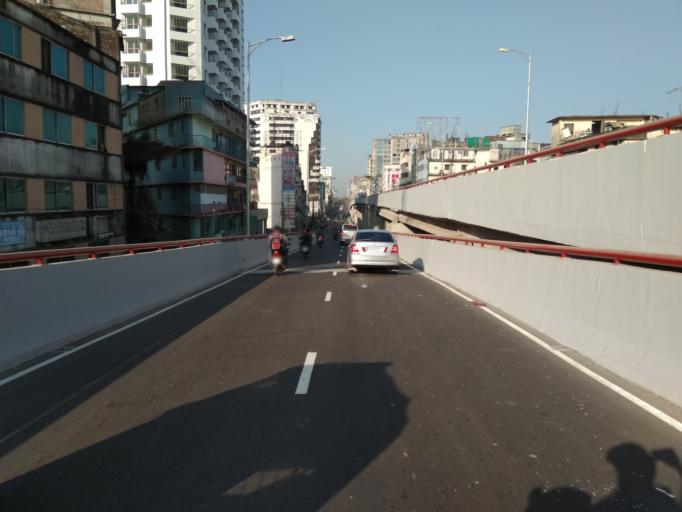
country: BD
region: Dhaka
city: Paltan
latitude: 23.7504
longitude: 90.4131
